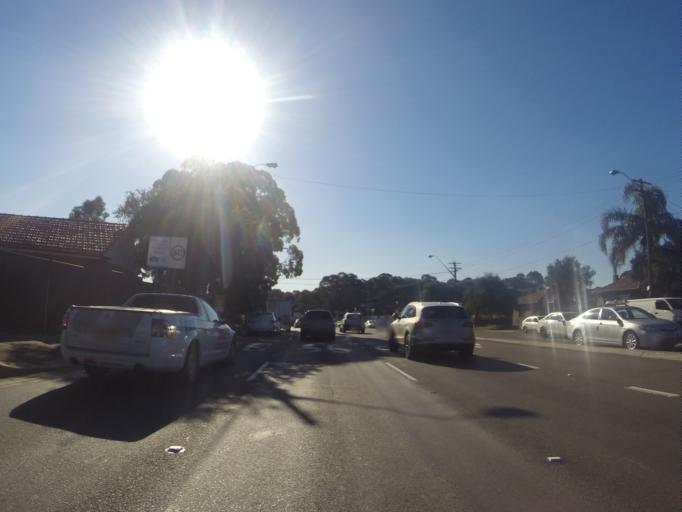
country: AU
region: New South Wales
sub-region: Canterbury
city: Roselands
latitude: -33.9307
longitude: 151.0727
